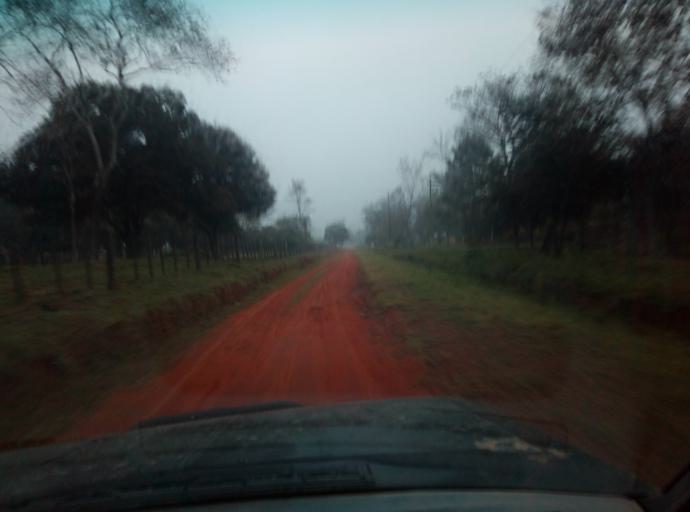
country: PY
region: Caaguazu
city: Doctor Cecilio Baez
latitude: -25.1567
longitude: -56.2778
